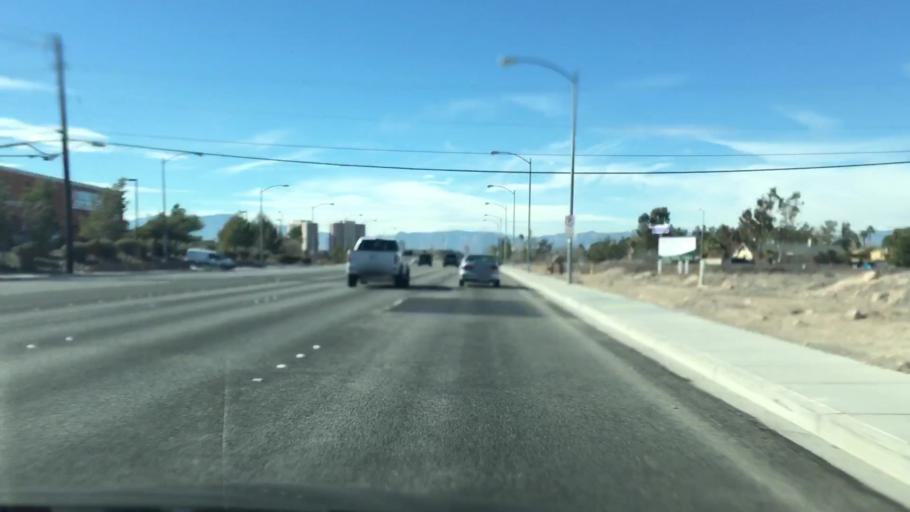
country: US
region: Nevada
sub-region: Clark County
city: Paradise
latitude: 36.0424
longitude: -115.1573
